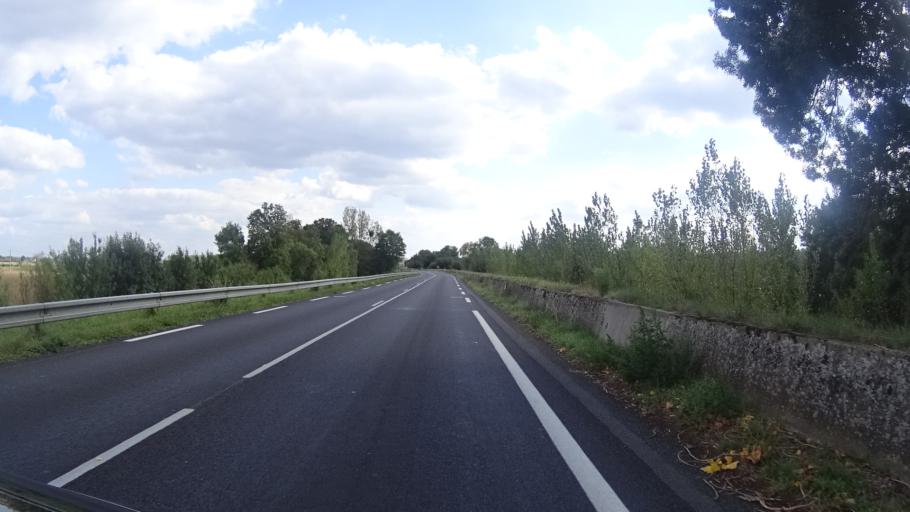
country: FR
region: Pays de la Loire
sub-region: Departement de Maine-et-Loire
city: Gennes
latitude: 47.3598
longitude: -0.2457
